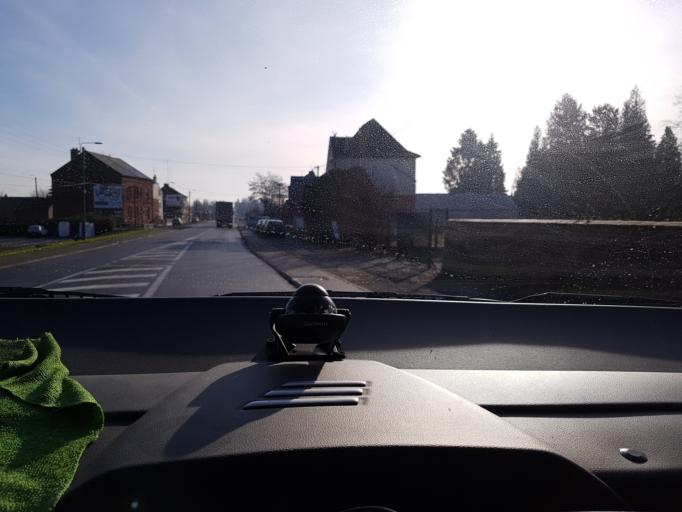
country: FR
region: Nord-Pas-de-Calais
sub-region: Departement du Nord
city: Avesnes-sur-Helpe
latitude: 50.1171
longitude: 3.9361
